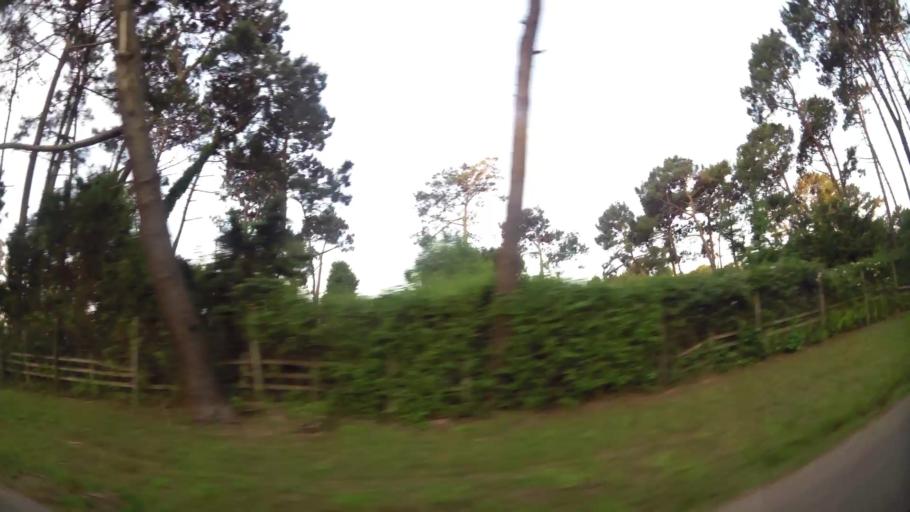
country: UY
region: Maldonado
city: Maldonado
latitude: -34.9306
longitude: -54.9358
